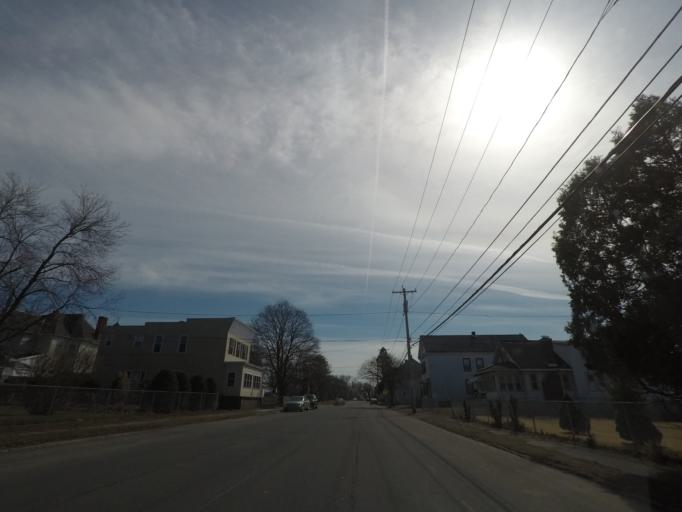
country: US
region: New York
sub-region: Albany County
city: Cohoes
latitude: 42.7691
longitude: -73.6894
